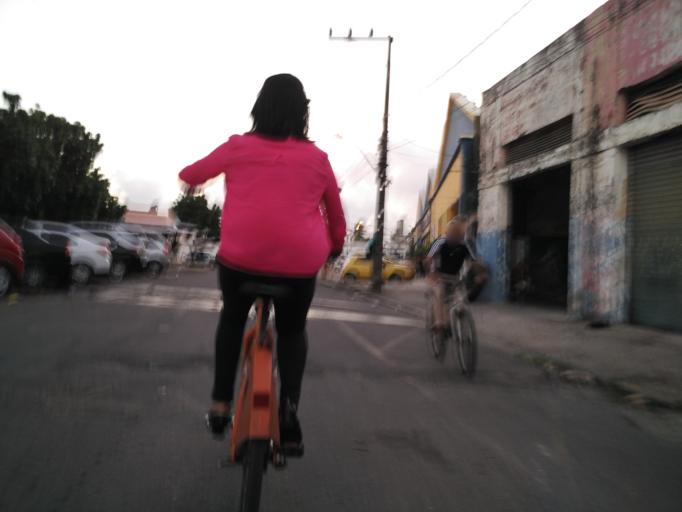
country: BR
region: Pernambuco
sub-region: Recife
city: Recife
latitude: -8.0709
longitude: -34.8774
